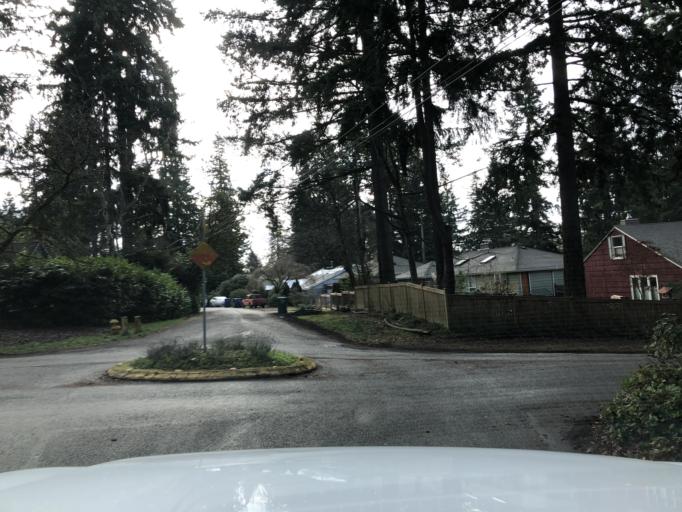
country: US
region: Washington
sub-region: King County
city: Lake Forest Park
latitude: 47.7286
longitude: -122.3044
